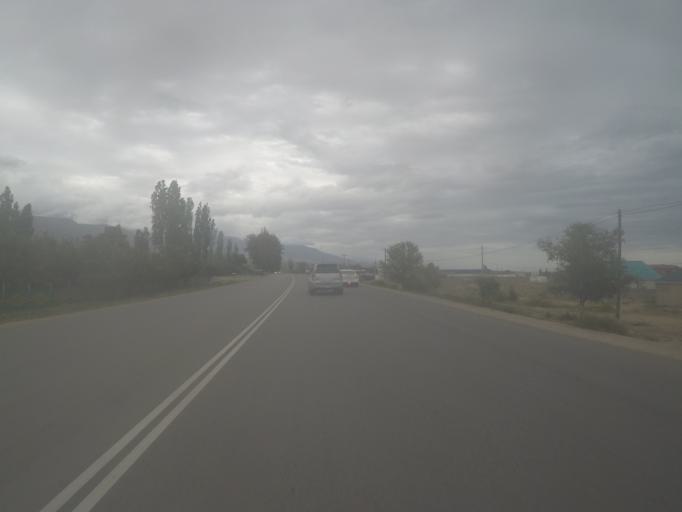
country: KG
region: Ysyk-Koel
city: Cholpon-Ata
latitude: 42.5887
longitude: 76.7480
